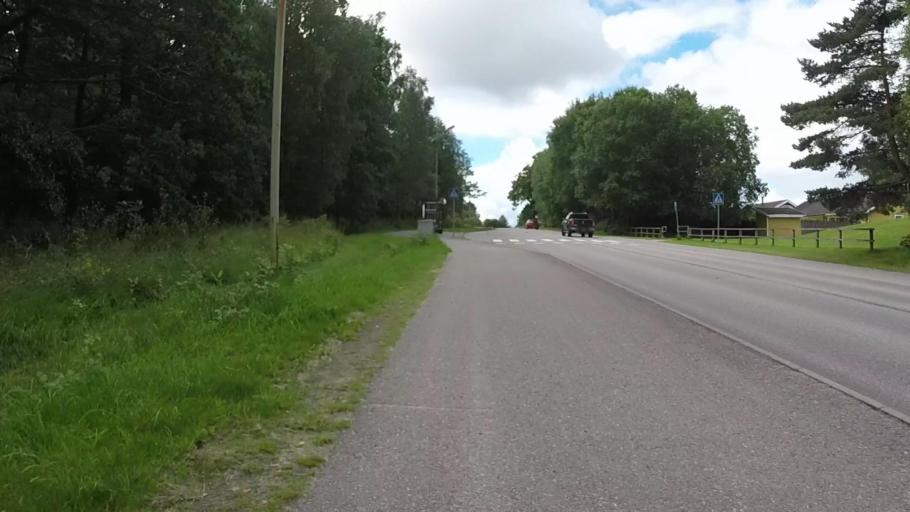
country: SE
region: Vaestra Goetaland
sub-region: Trollhattan
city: Trollhattan
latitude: 58.2917
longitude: 12.2779
